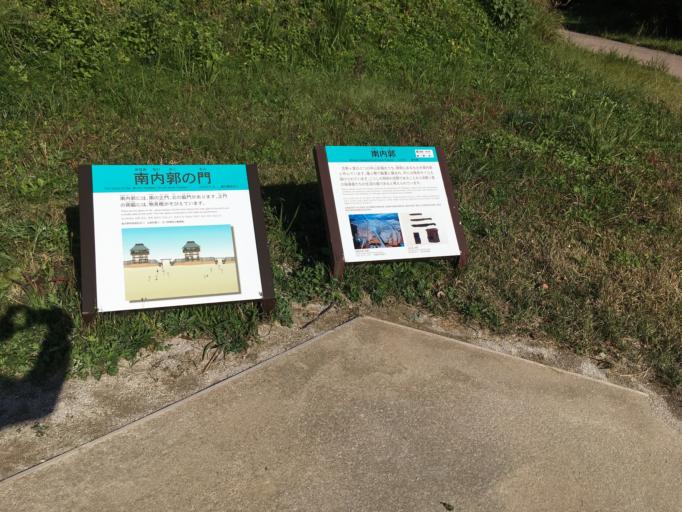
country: JP
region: Saga Prefecture
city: Kanzakimachi-kanzaki
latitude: 33.3247
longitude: 130.3851
